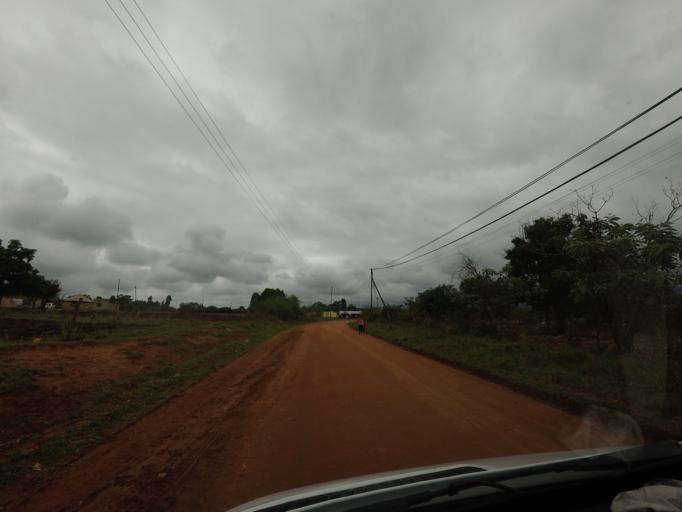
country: SZ
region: Hhohho
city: Lobamba
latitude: -26.4710
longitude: 31.2063
